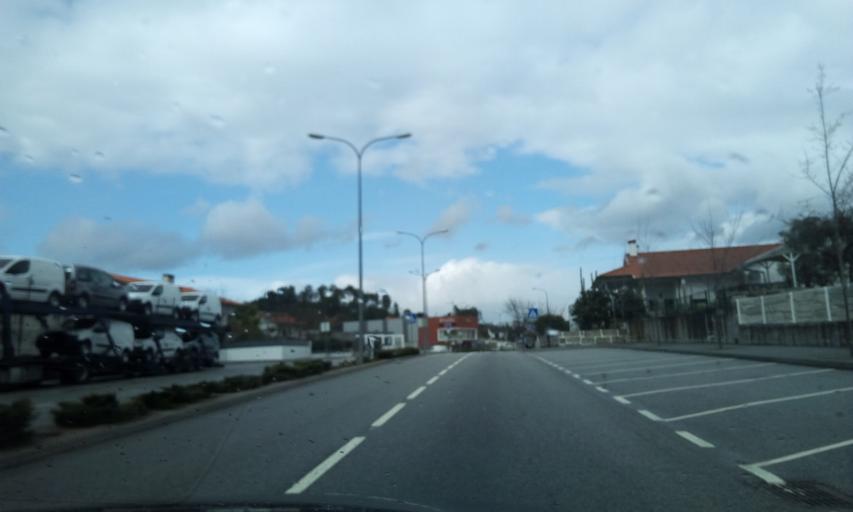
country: PT
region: Viseu
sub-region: Viseu
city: Viseu
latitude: 40.6268
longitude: -7.9146
